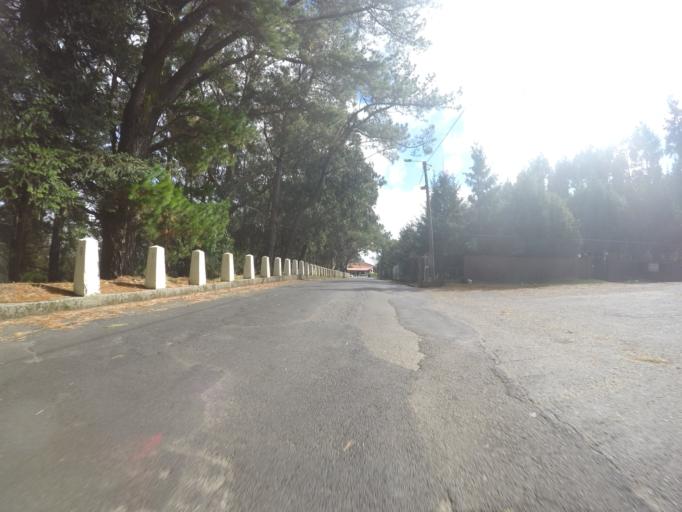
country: PT
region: Madeira
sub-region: Funchal
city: Nossa Senhora do Monte
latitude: 32.6960
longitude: -16.8783
